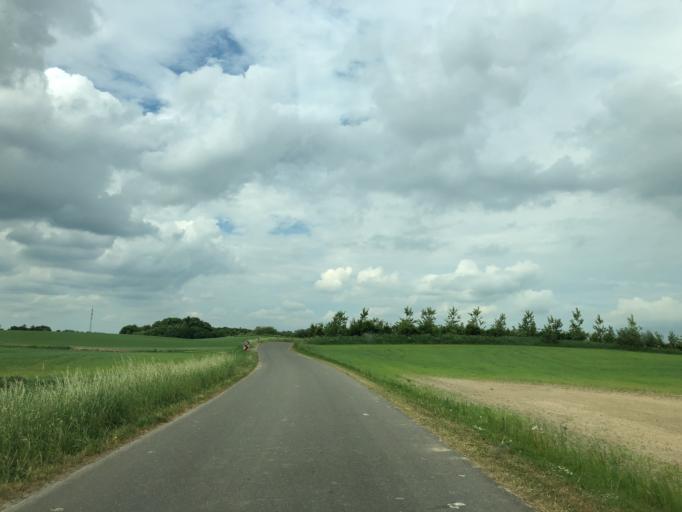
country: DK
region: Central Jutland
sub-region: Struer Kommune
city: Struer
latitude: 56.4667
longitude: 8.5668
